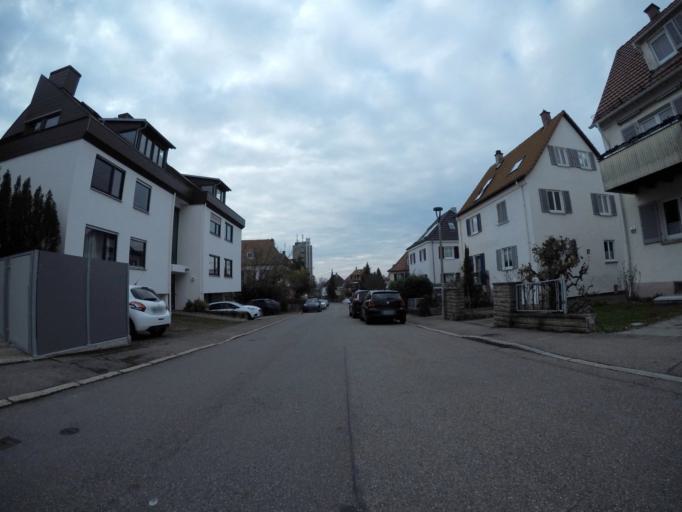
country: DE
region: Baden-Wuerttemberg
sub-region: Tuebingen Region
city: Reutlingen
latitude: 48.5014
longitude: 9.2237
